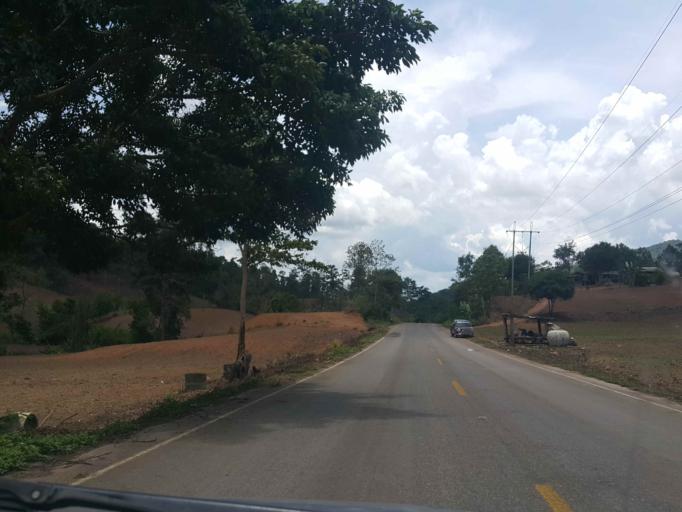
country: TH
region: Phayao
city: Chiang Muan
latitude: 18.9064
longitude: 100.1199
